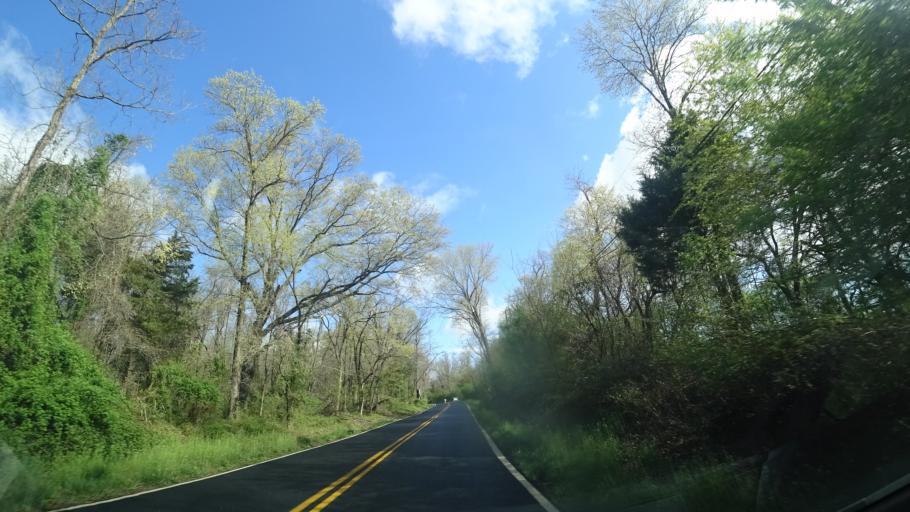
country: US
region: Maryland
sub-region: Montgomery County
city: Poolesville
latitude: 39.1202
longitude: -77.3810
